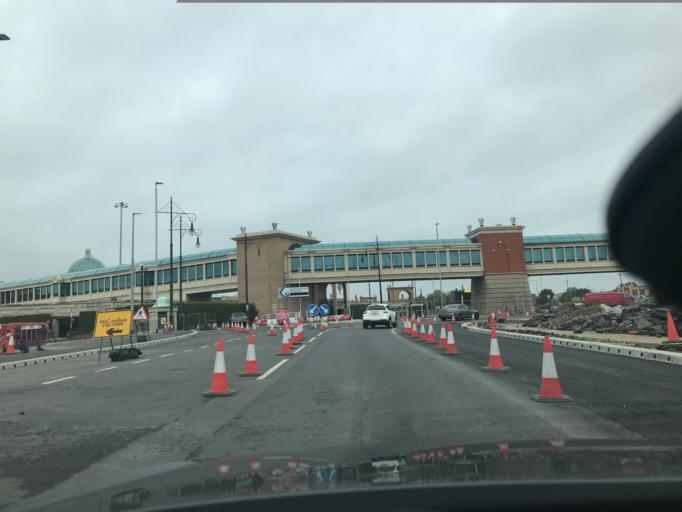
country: GB
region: England
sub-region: Trafford
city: Urmston
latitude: 53.4650
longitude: -2.3423
